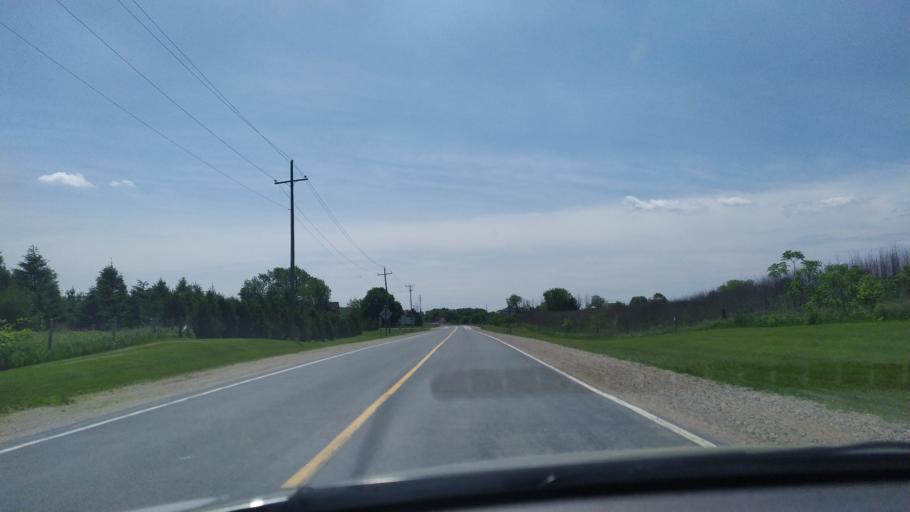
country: CA
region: Ontario
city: Ingersoll
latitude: 43.0056
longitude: -80.9607
